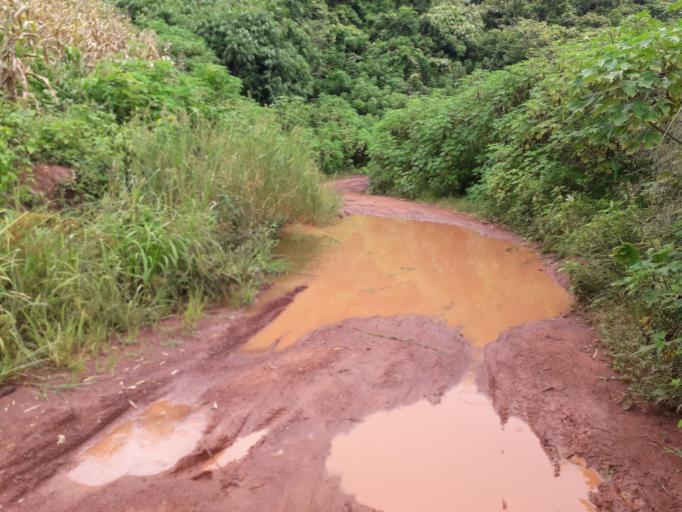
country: CN
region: Yunnan
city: Menglie
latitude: 22.2412
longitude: 101.6150
